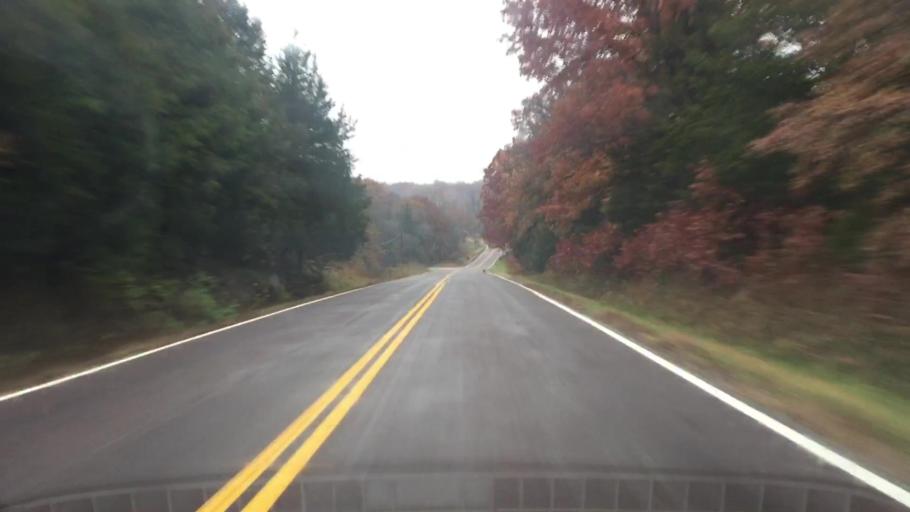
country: US
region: Missouri
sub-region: Boone County
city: Columbia
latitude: 38.8731
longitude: -92.3238
